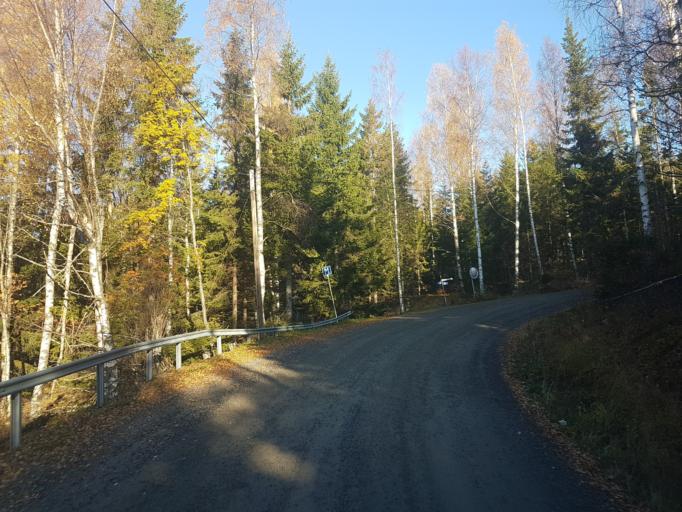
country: SE
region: Vaesternorrland
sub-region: OErnskoeldsviks Kommun
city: Bjasta
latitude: 63.0717
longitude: 18.4301
